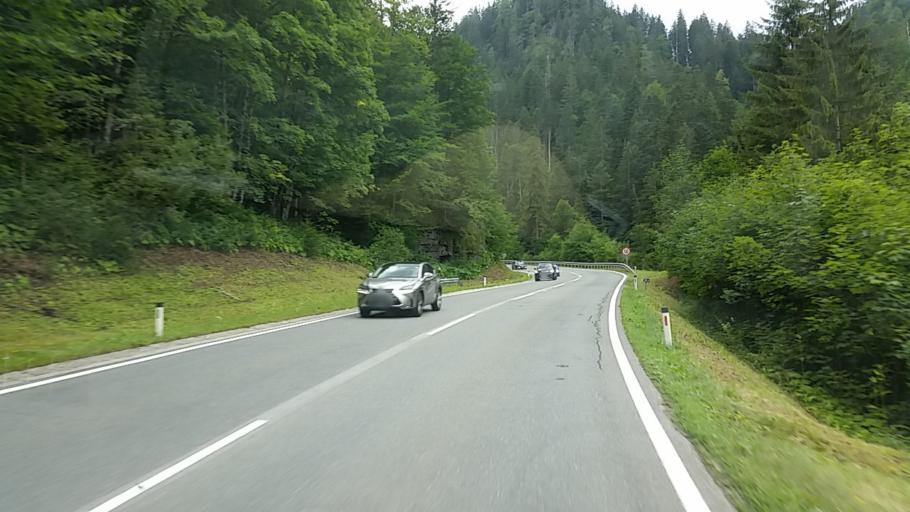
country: AT
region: Salzburg
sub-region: Politischer Bezirk Sankt Johann im Pongau
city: Untertauern
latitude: 47.2801
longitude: 13.5044
